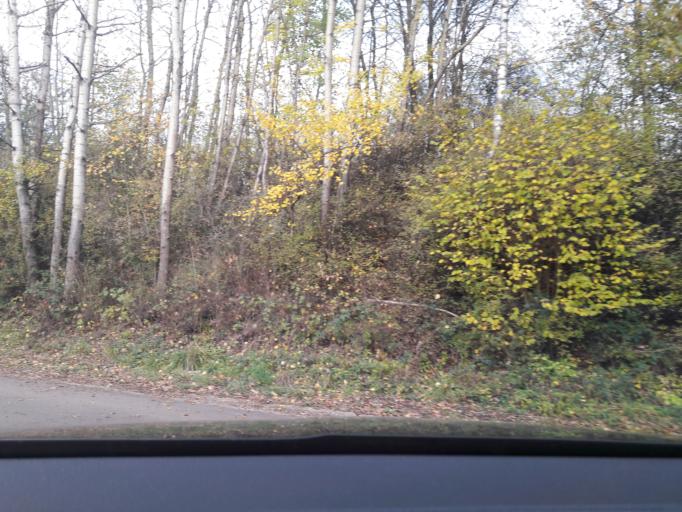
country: DE
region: Saarland
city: Sankt Wendel
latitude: 49.4518
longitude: 7.1772
